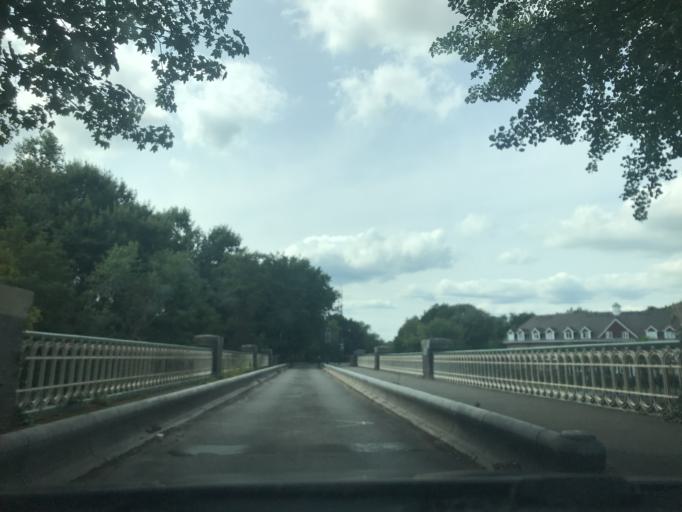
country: GB
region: England
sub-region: Surrey
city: Weybridge
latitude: 51.3715
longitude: -0.4652
